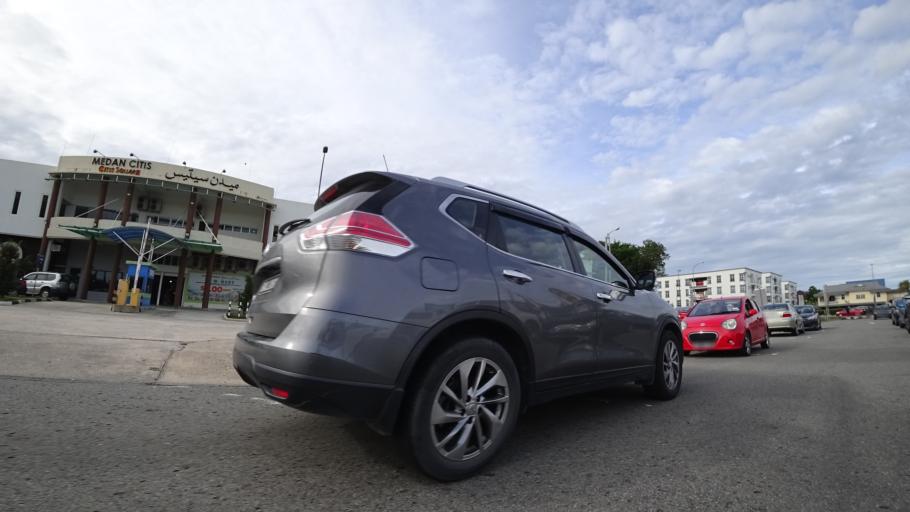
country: BN
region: Brunei and Muara
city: Bandar Seri Begawan
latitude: 4.9383
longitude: 114.9401
